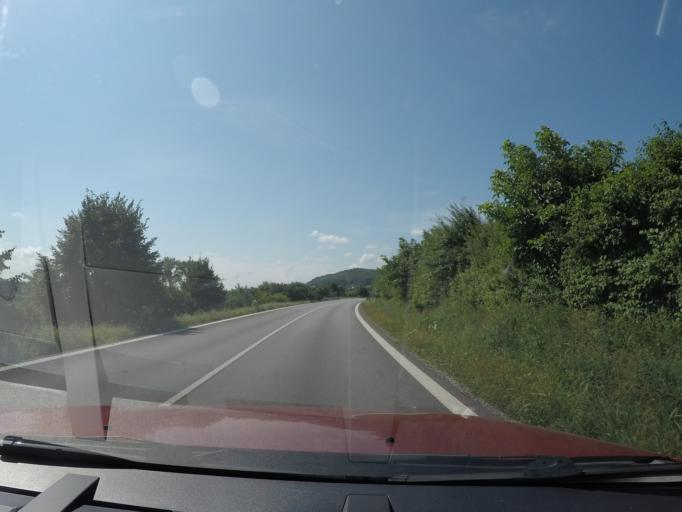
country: SK
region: Presovsky
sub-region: Okres Presov
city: Presov
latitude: 48.9101
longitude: 21.2412
